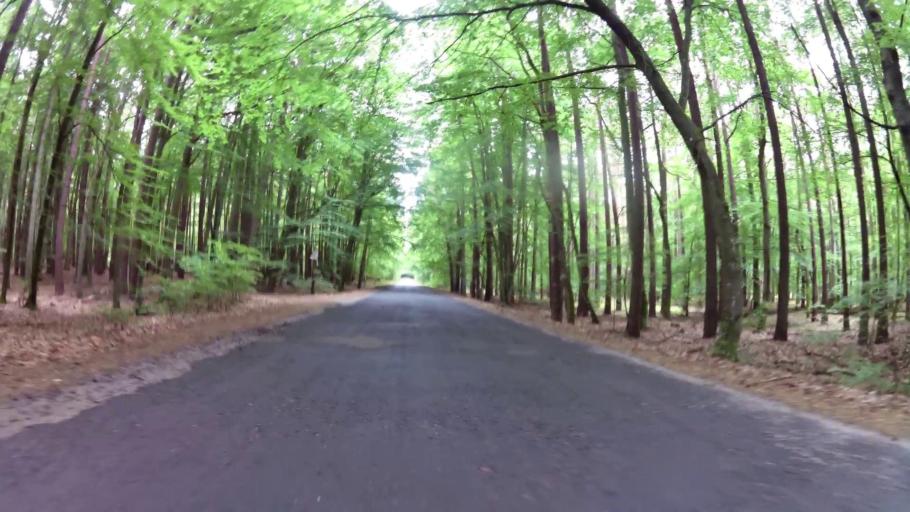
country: PL
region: West Pomeranian Voivodeship
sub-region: Powiat kamienski
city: Miedzyzdroje
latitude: 53.9436
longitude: 14.5512
